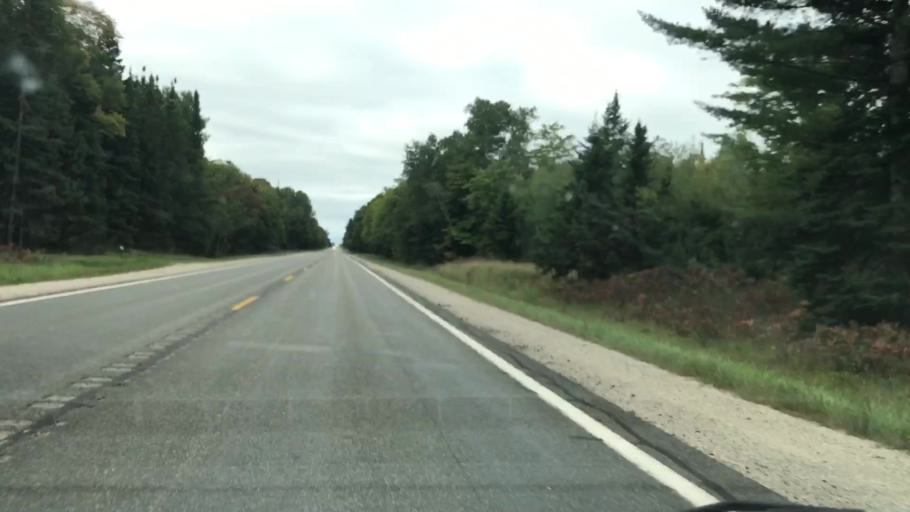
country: US
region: Michigan
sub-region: Luce County
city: Newberry
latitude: 46.2306
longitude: -85.5721
